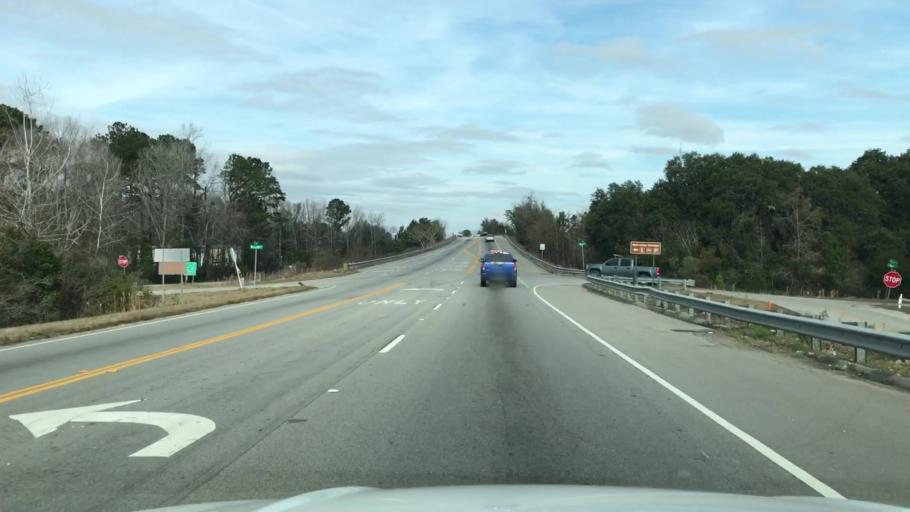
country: US
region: South Carolina
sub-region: Charleston County
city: Shell Point
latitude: 32.7902
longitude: -80.1080
